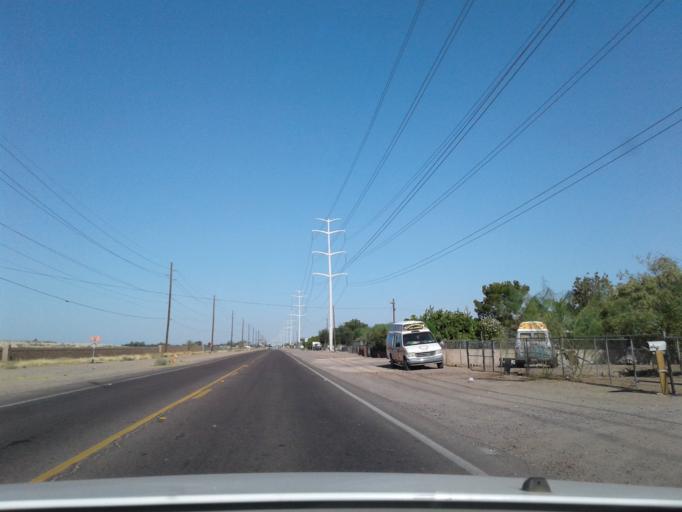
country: US
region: Arizona
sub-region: Maricopa County
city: Laveen
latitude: 33.4083
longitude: -112.1958
